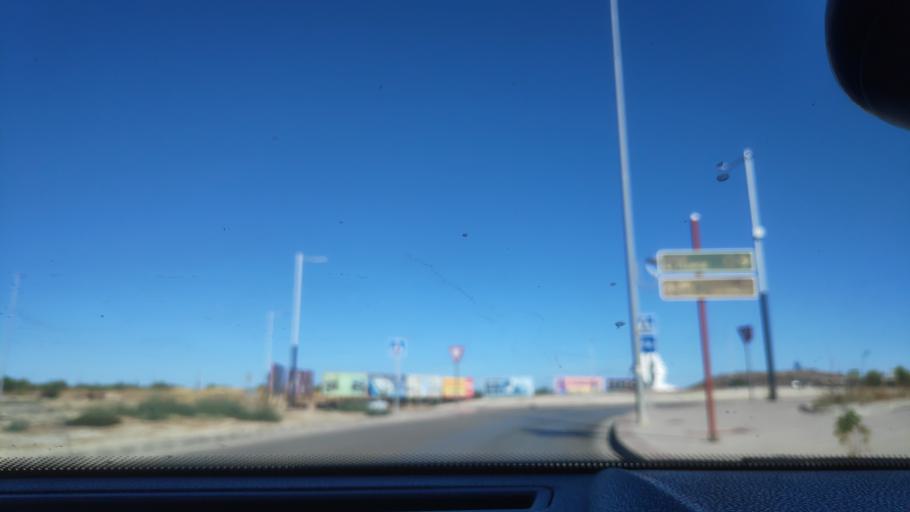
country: ES
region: Andalusia
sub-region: Provincia de Jaen
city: Jaen
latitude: 37.7910
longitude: -3.7910
